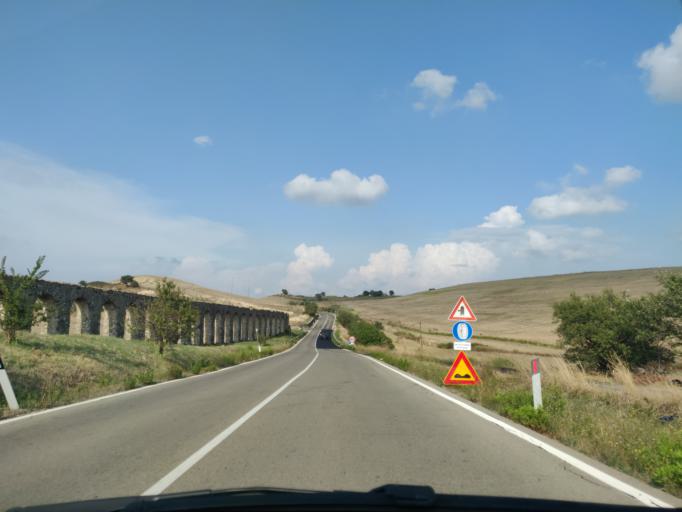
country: IT
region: Latium
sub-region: Provincia di Viterbo
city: Tarquinia
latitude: 42.2549
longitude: 11.8159
